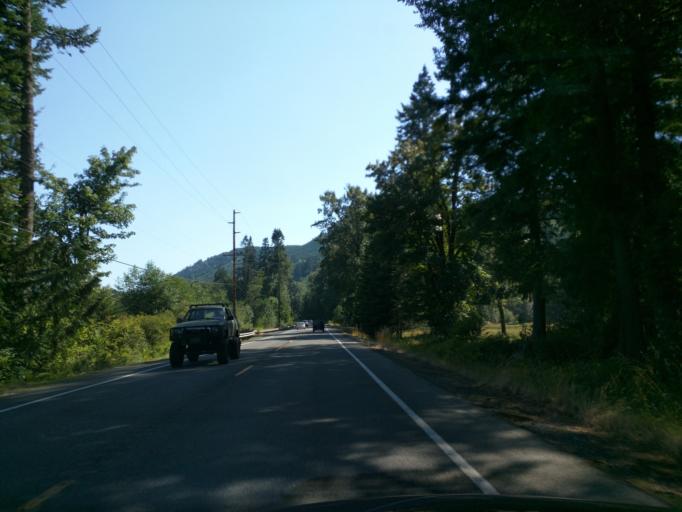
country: US
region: Washington
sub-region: Whatcom County
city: Peaceful Valley
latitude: 48.8848
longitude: -122.1548
